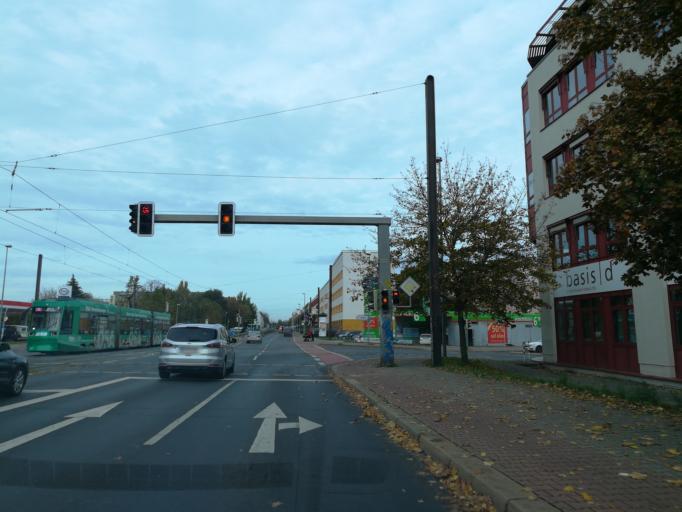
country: DE
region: Saxony-Anhalt
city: Magdeburg
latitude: 52.1230
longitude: 11.6066
